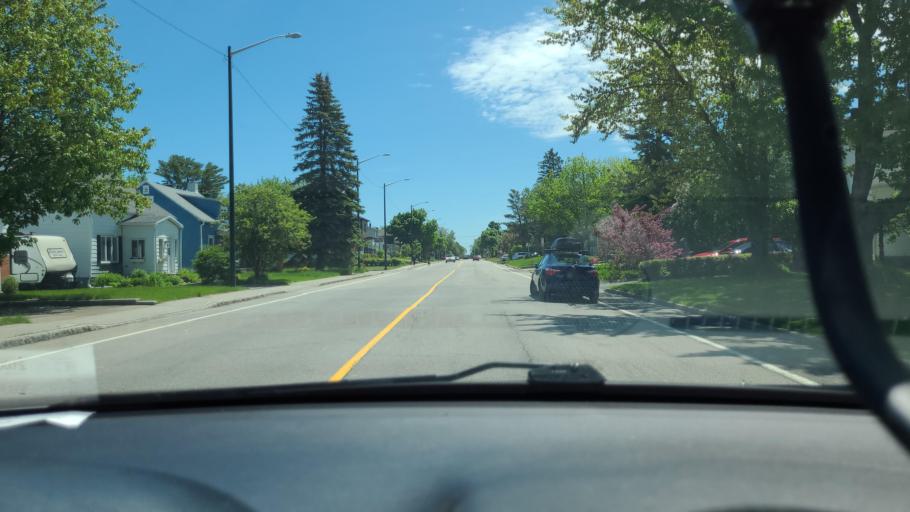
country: CA
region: Quebec
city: L'Ancienne-Lorette
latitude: 46.7624
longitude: -71.3234
